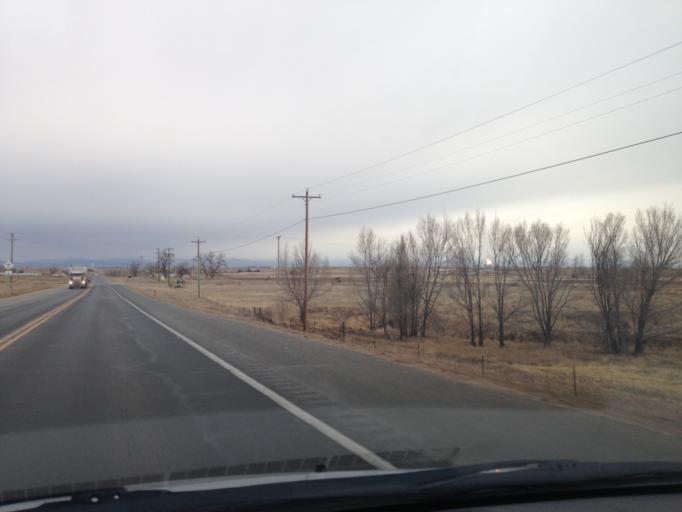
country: US
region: Colorado
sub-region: Weld County
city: Fort Lupton
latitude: 40.0800
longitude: -104.8651
